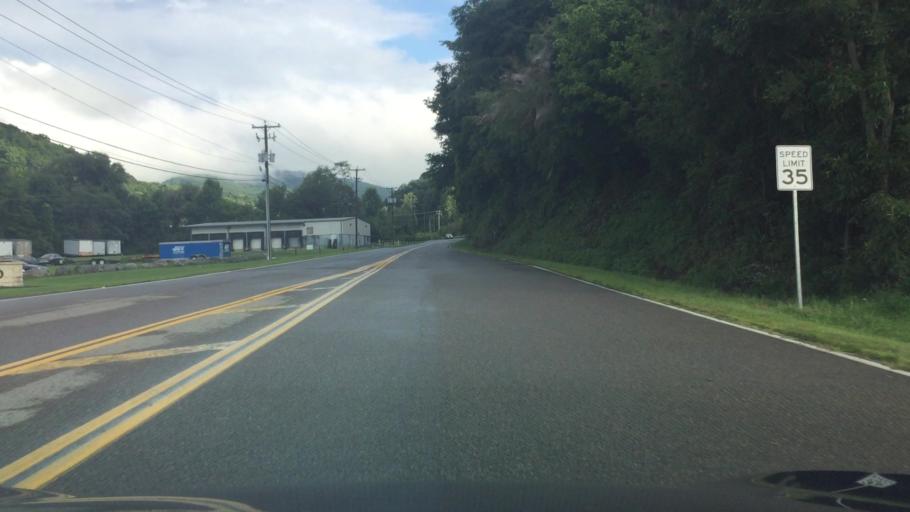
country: US
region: Virginia
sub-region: Smyth County
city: Atkins
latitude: 36.8602
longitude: -81.4325
